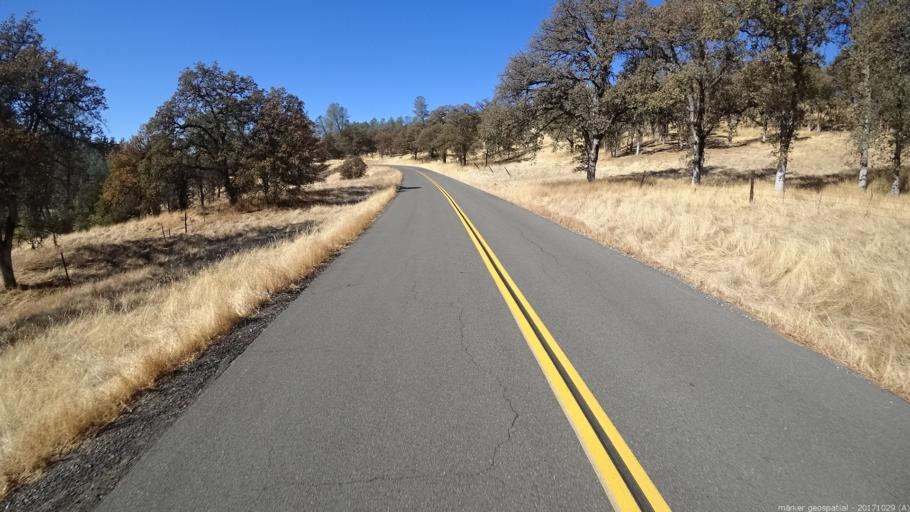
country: US
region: California
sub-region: Shasta County
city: Shasta
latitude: 40.4293
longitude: -122.7192
